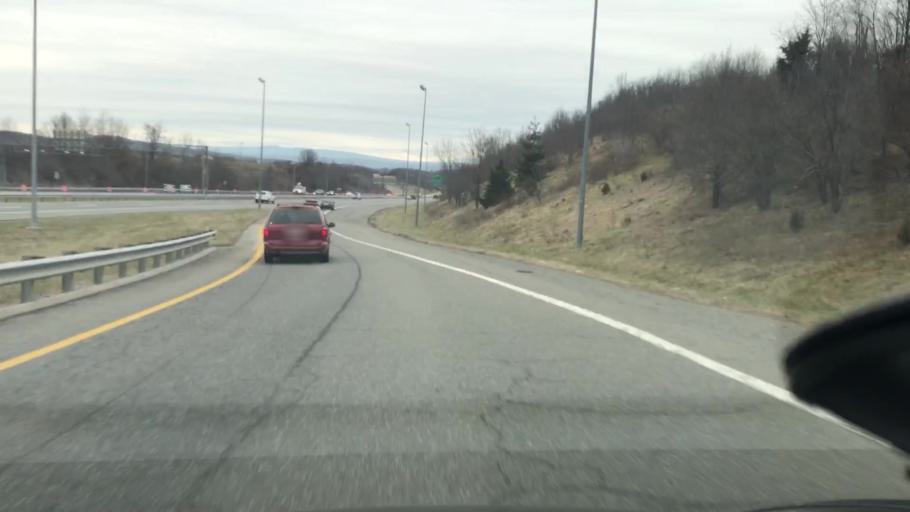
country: US
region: Virginia
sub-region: Montgomery County
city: Christiansburg
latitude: 37.1574
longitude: -80.4122
